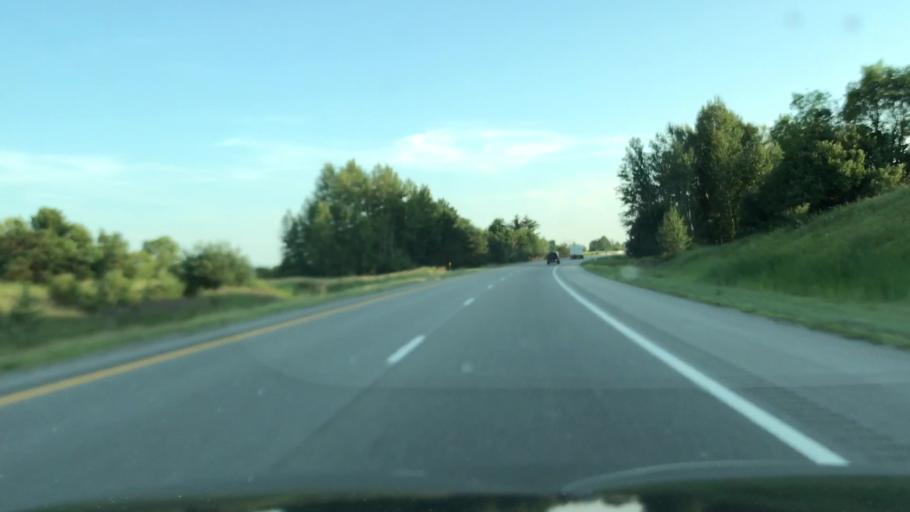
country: US
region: Michigan
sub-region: Osceola County
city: Reed City
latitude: 43.8777
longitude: -85.5286
